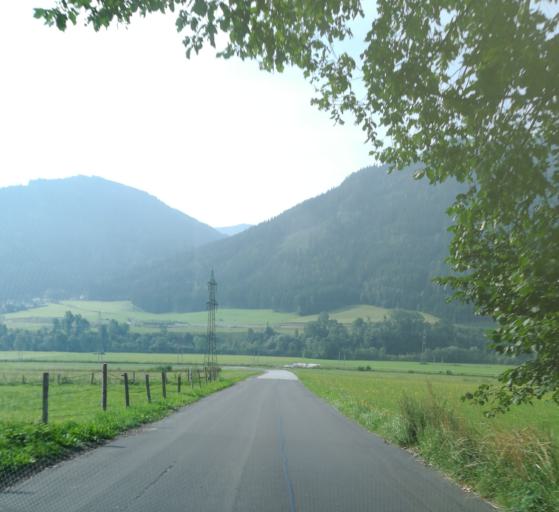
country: AT
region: Styria
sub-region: Politischer Bezirk Murtal
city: Sankt Georgen ob Judenburg
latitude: 47.2147
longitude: 14.4889
